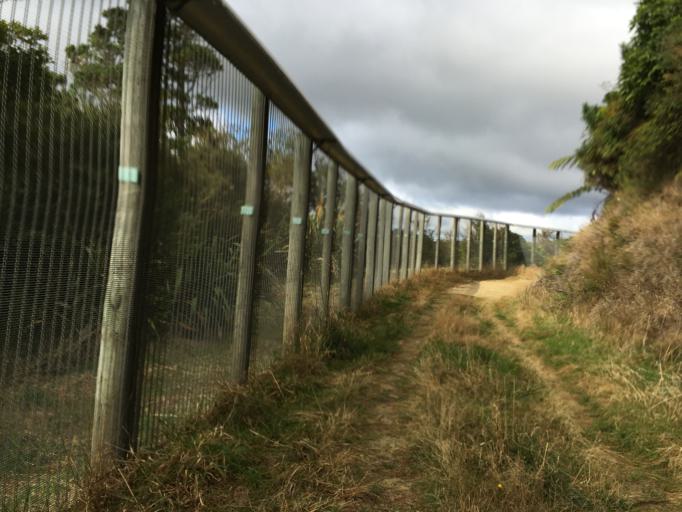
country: NZ
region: Wellington
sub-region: Wellington City
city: Brooklyn
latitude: -41.2985
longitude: 174.7389
